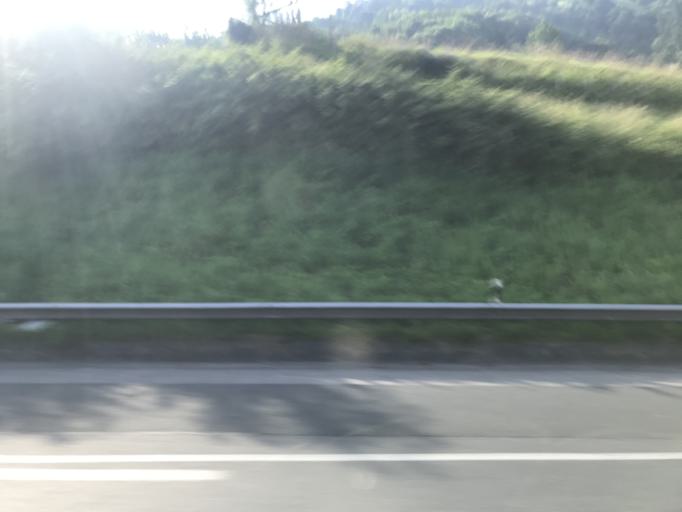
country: ES
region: Basque Country
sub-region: Provincia de Guipuzcoa
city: Villabona
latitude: 43.1793
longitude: -2.0542
